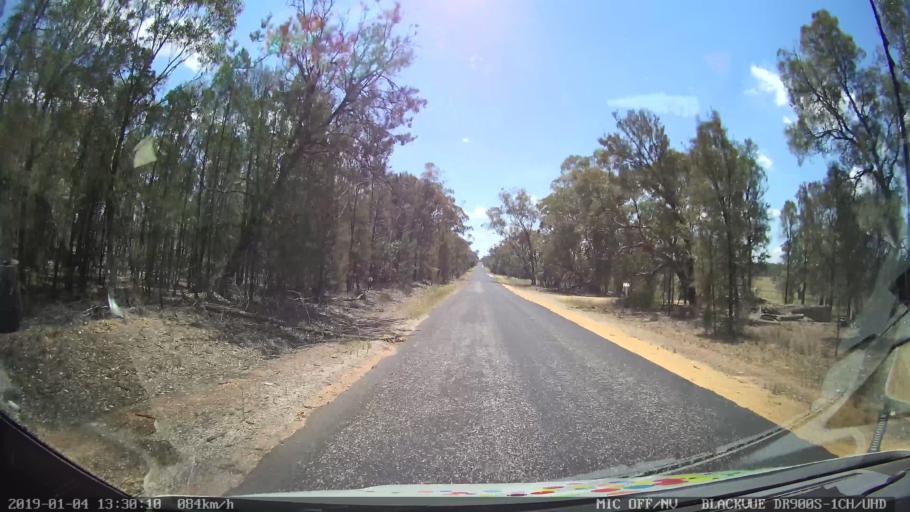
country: AU
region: New South Wales
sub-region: Parkes
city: Peak Hill
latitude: -32.6386
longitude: 148.5497
